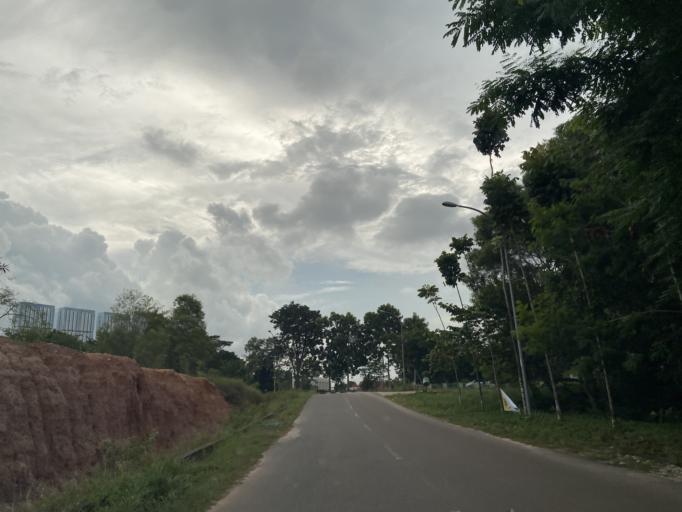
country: SG
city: Singapore
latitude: 1.1239
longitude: 104.0529
